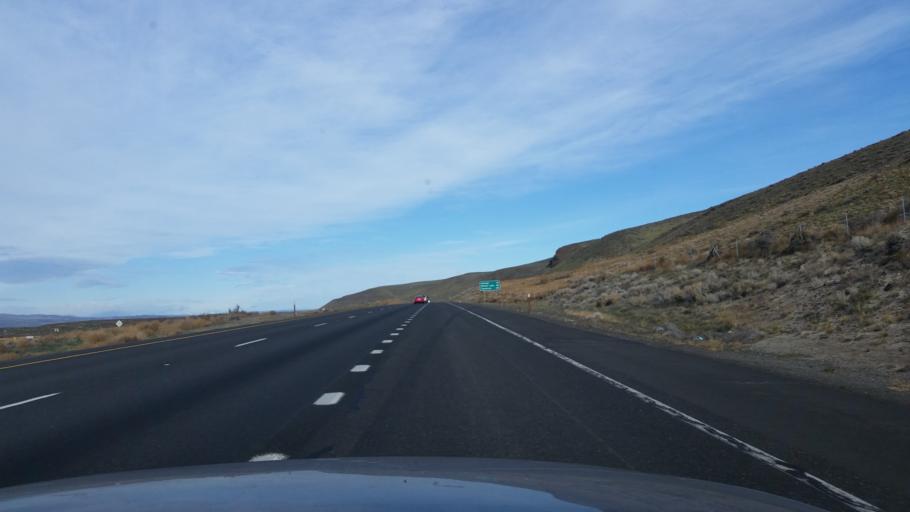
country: US
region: Washington
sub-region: Grant County
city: Mattawa
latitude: 46.9720
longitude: -119.9673
